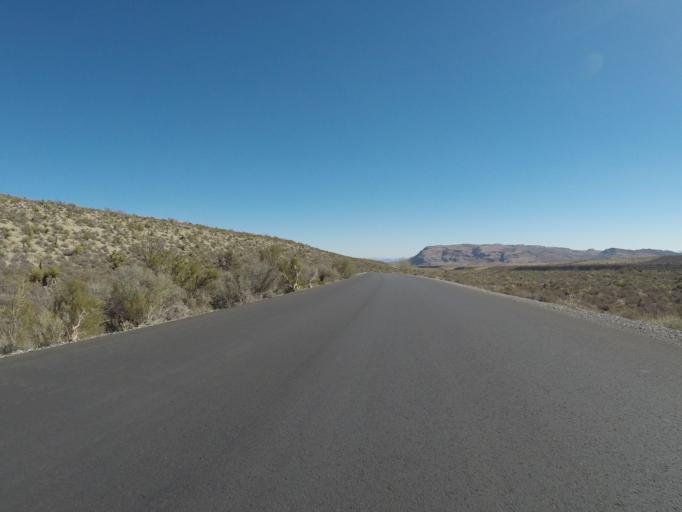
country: US
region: Nevada
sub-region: Clark County
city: Summerlin South
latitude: 36.1473
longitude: -115.4788
